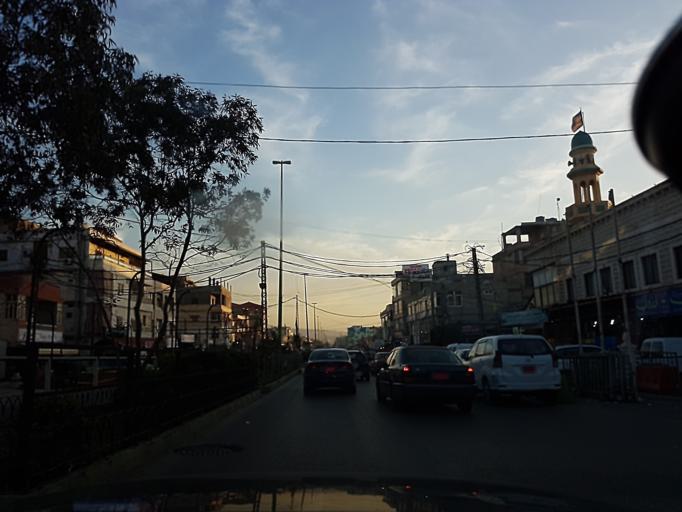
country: LB
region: Beyrouth
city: Beirut
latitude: 33.8441
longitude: 35.4849
